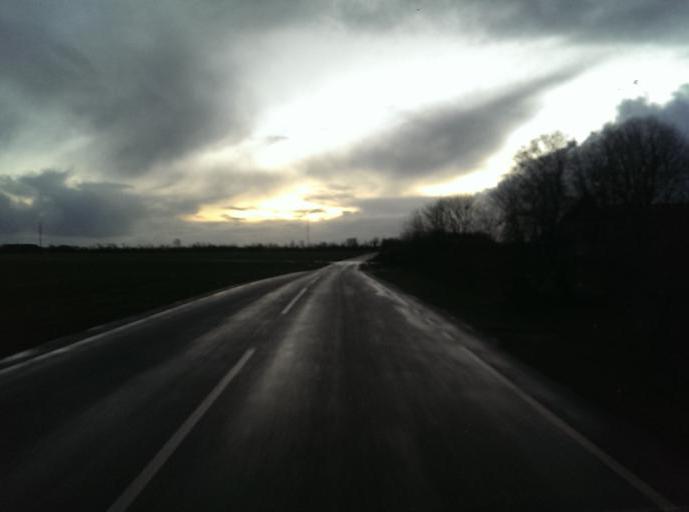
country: DK
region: South Denmark
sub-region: Esbjerg Kommune
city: Bramming
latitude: 55.4365
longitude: 8.6837
